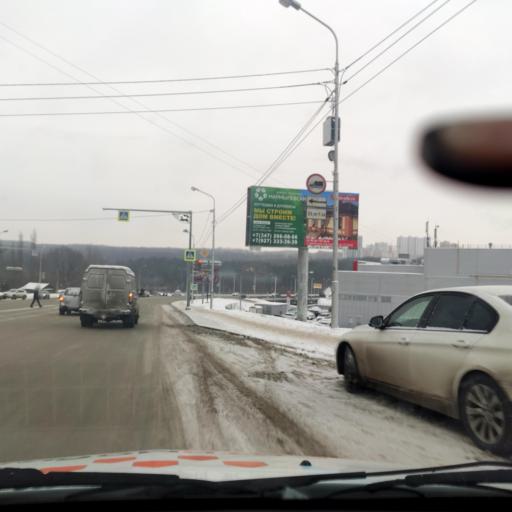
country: RU
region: Bashkortostan
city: Ufa
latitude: 54.7308
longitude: 55.9948
